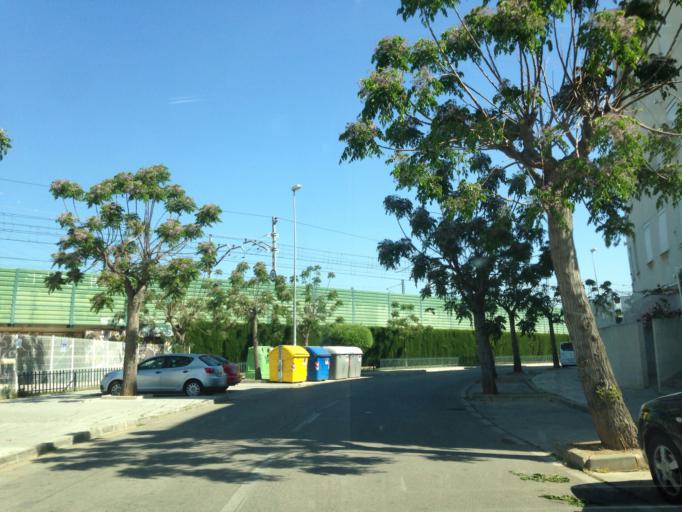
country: ES
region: Andalusia
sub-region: Provincia de Malaga
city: Malaga
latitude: 36.6961
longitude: -4.4641
